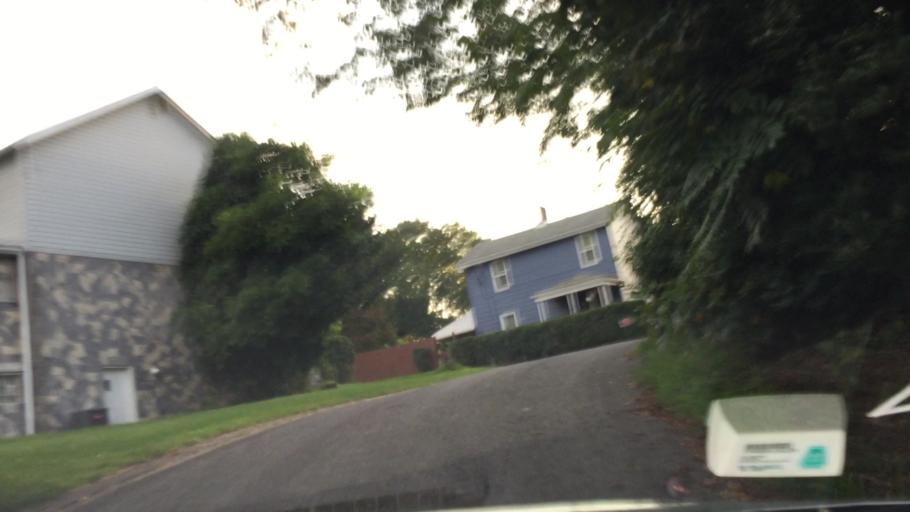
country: US
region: Pennsylvania
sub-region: Allegheny County
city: Imperial
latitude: 40.4329
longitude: -80.2711
